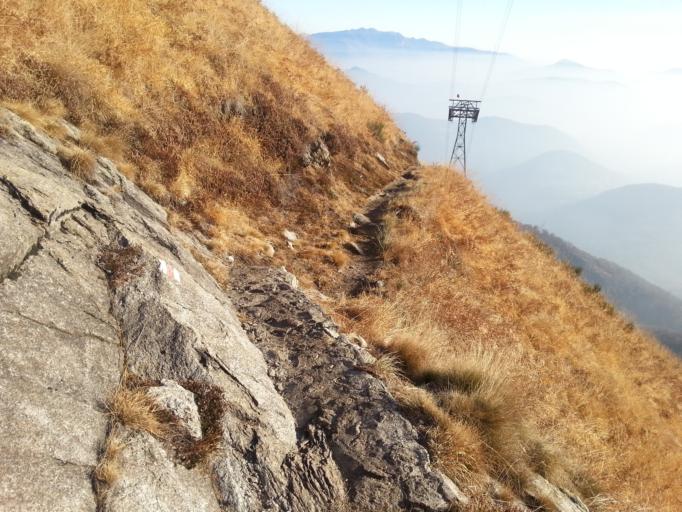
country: IT
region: Lombardy
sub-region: Provincia di Varese
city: Curiglia
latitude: 46.0393
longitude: 8.8367
